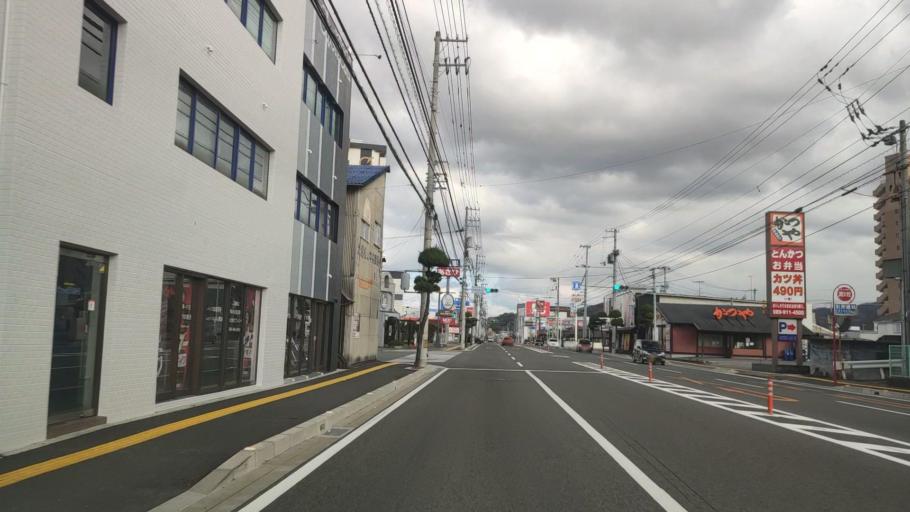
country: JP
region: Ehime
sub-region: Shikoku-chuo Shi
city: Matsuyama
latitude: 33.8615
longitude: 132.7495
